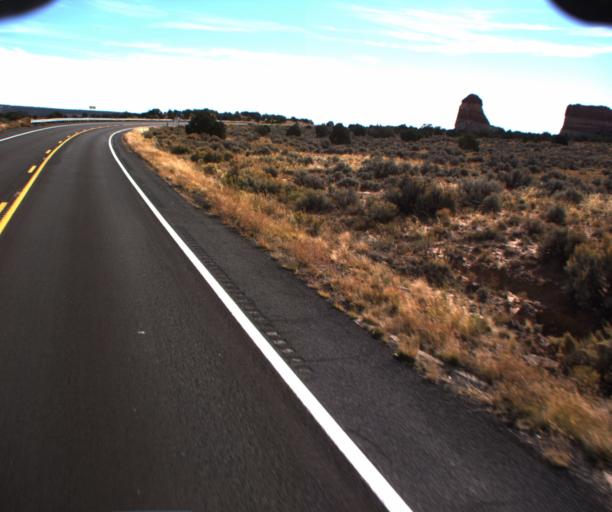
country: US
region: Arizona
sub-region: Coconino County
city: Kaibito
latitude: 36.6143
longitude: -110.9274
